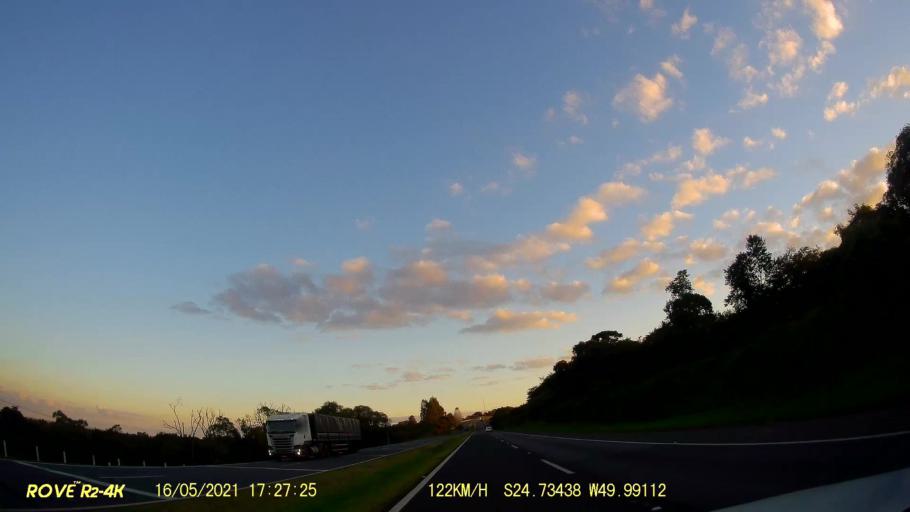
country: BR
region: Parana
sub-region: Castro
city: Castro
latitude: -24.7348
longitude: -49.9913
